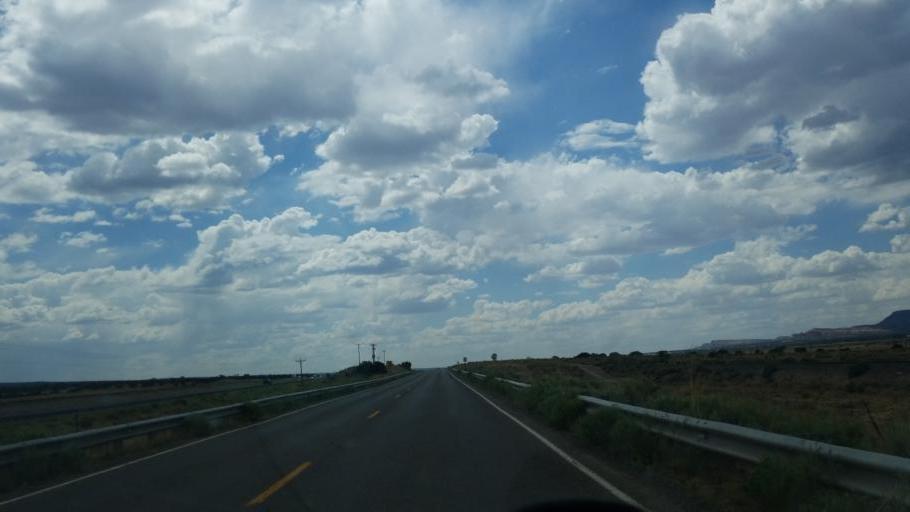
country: US
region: New Mexico
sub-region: McKinley County
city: Thoreau
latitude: 35.3885
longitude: -108.1592
